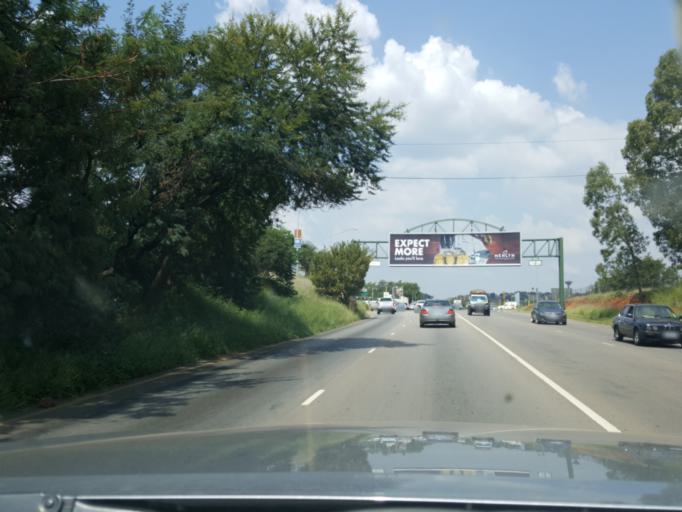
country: ZA
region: Gauteng
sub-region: City of Tshwane Metropolitan Municipality
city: Centurion
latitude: -25.8151
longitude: 28.2402
